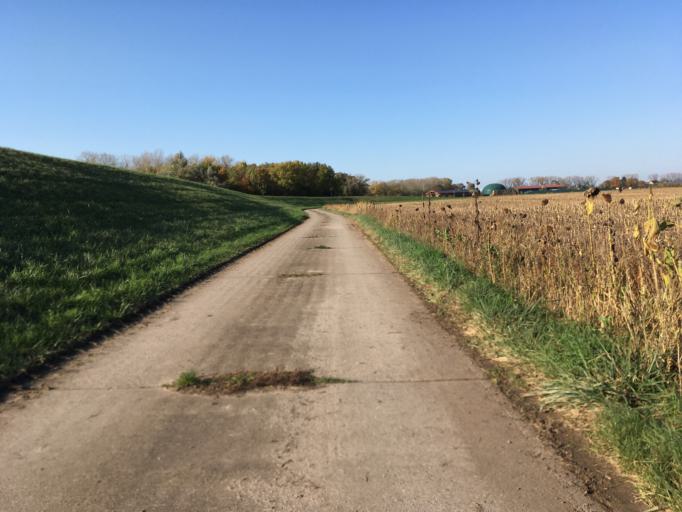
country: DE
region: Rheinland-Pfalz
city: Worms
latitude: 49.6809
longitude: 8.3676
